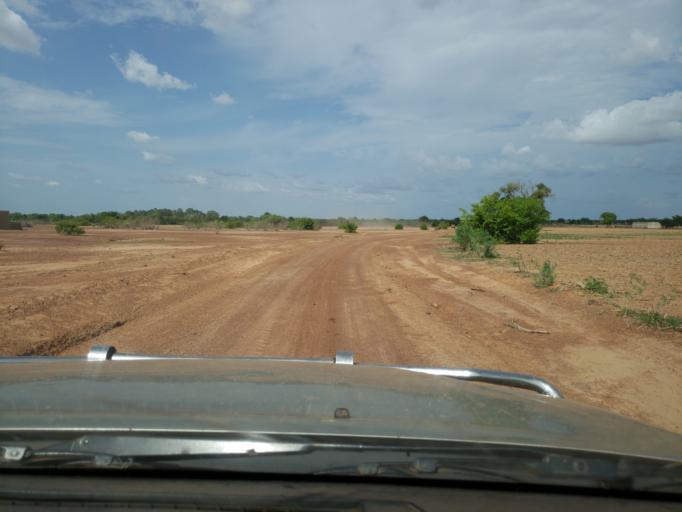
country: ML
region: Segou
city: Bla
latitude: 12.7435
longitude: -5.6455
